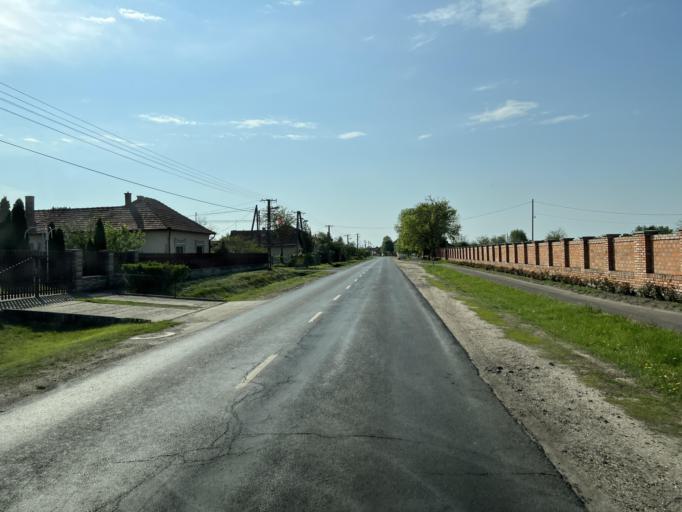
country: HU
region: Pest
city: Jaszkarajeno
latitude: 47.0602
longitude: 20.0588
